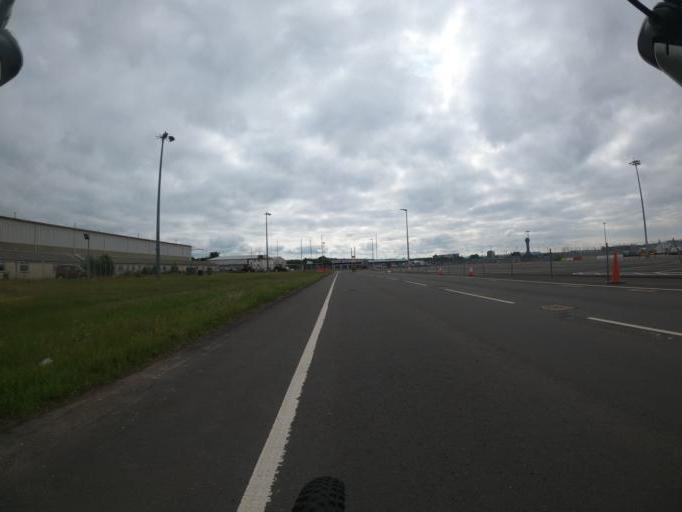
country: GB
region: Scotland
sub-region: Edinburgh
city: Ratho
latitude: 55.9452
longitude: -3.3500
